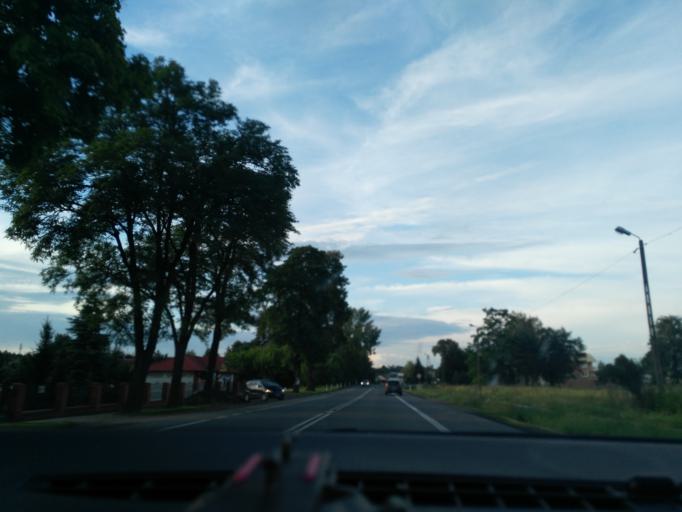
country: PL
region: Lublin Voivodeship
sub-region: Powiat lubelski
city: Niedrzwica Duza
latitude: 51.1025
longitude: 22.3730
